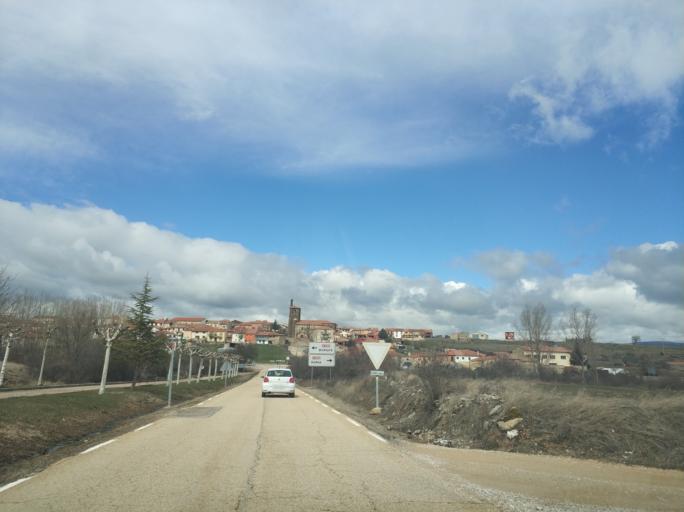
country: ES
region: Castille and Leon
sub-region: Provincia de Soria
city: Abejar
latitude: 41.8049
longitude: -2.7814
